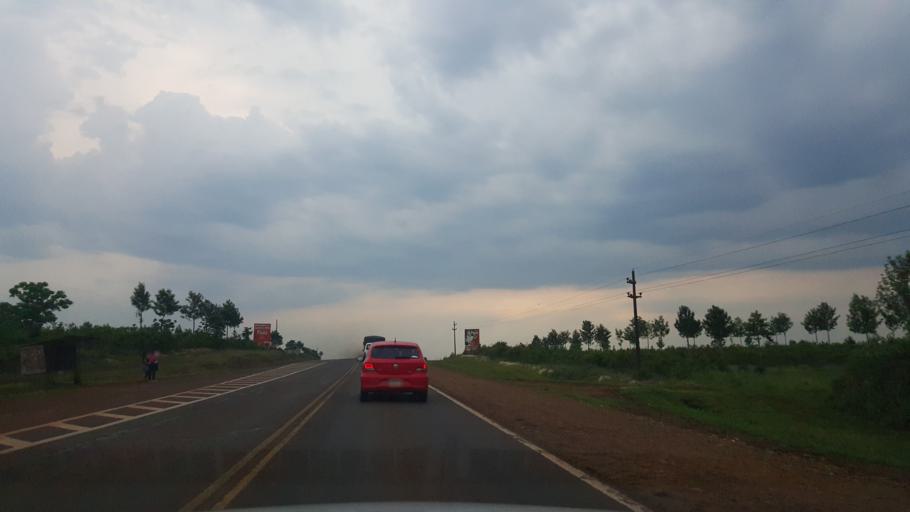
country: AR
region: Misiones
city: Gobernador Roca
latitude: -27.1664
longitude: -55.4411
